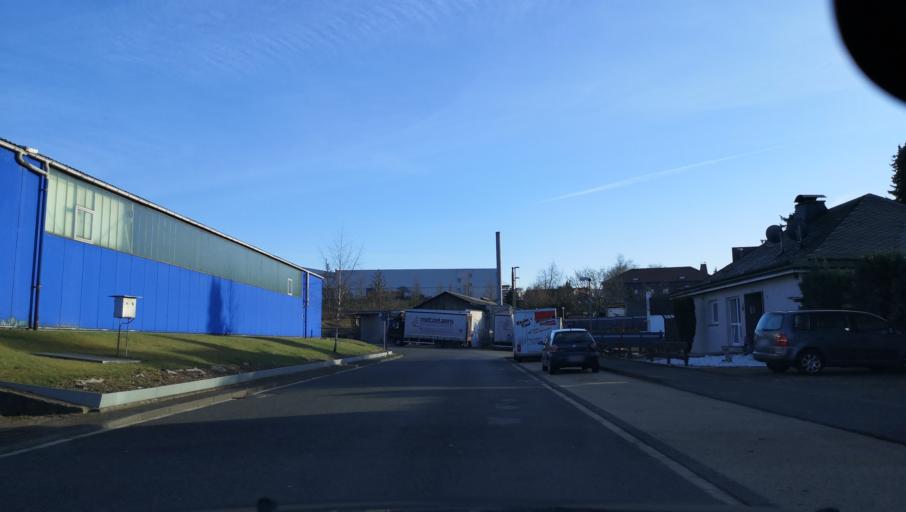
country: DE
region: North Rhine-Westphalia
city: Radevormwald
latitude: 51.2047
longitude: 7.3717
